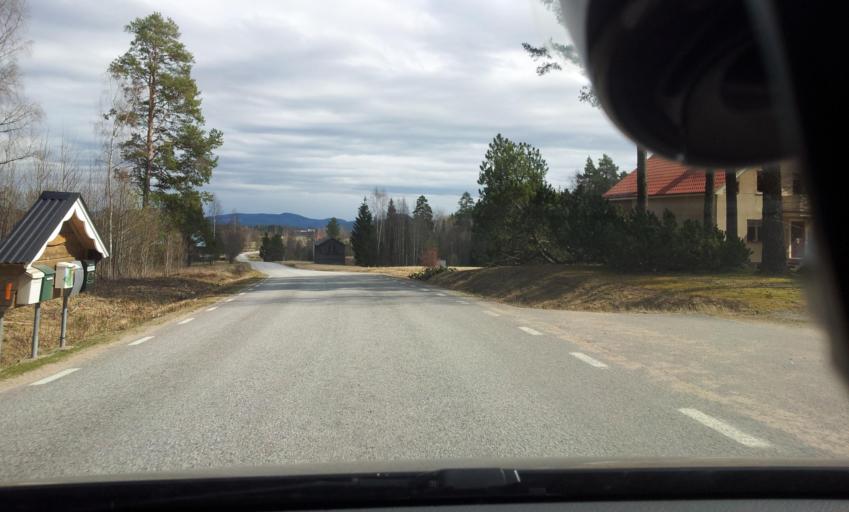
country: SE
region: Gaevleborg
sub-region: Ljusdals Kommun
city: Ljusdal
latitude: 61.7677
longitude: 16.0258
